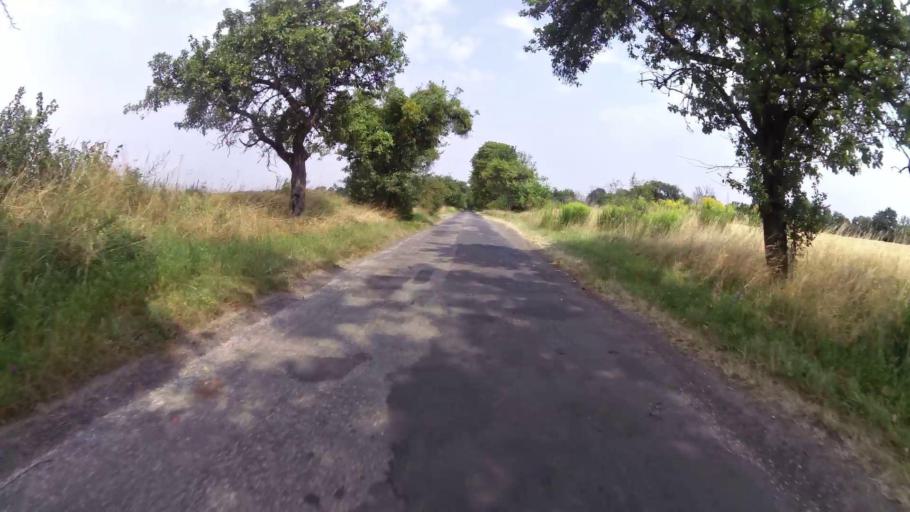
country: PL
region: West Pomeranian Voivodeship
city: Trzcinsko Zdroj
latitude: 52.8969
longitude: 14.5292
